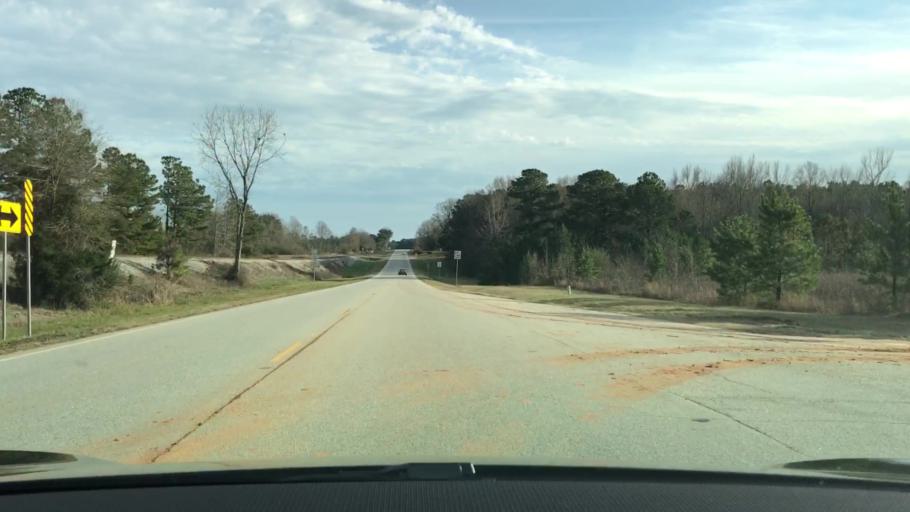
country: US
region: Georgia
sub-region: Taliaferro County
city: Crawfordville
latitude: 33.4971
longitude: -82.8029
